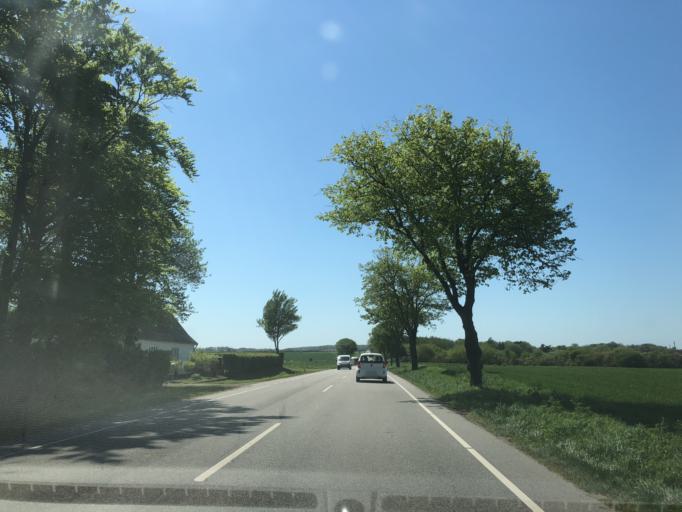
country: DK
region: Zealand
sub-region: Slagelse Kommune
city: Forlev
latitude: 55.3387
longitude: 11.2185
